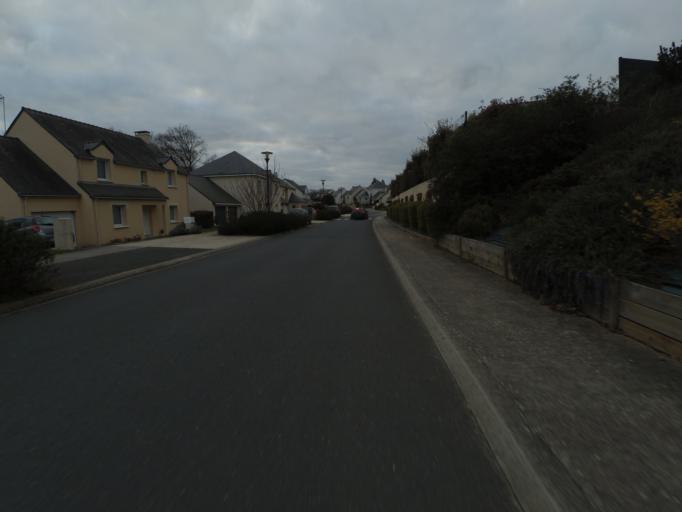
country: FR
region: Pays de la Loire
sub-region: Departement de la Loire-Atlantique
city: Carquefou
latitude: 47.3075
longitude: -1.4866
